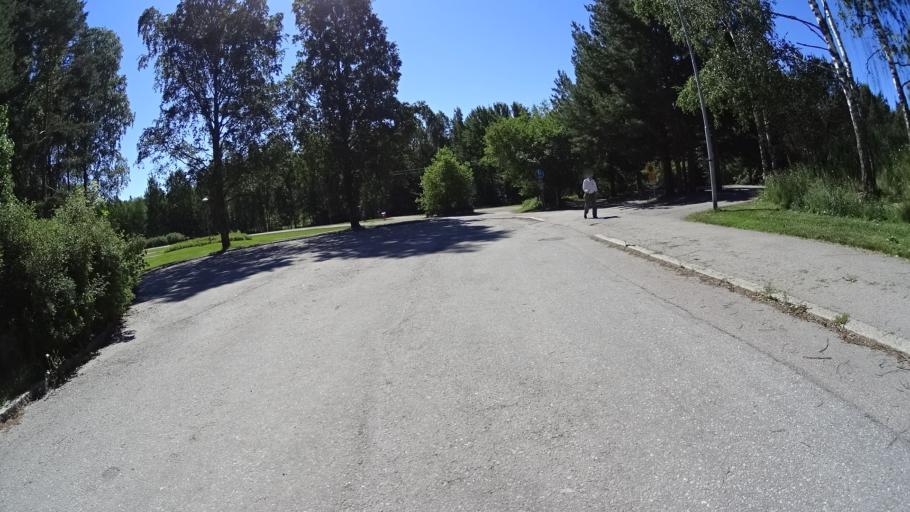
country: FI
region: Uusimaa
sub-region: Helsinki
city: Espoo
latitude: 60.1476
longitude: 24.6925
